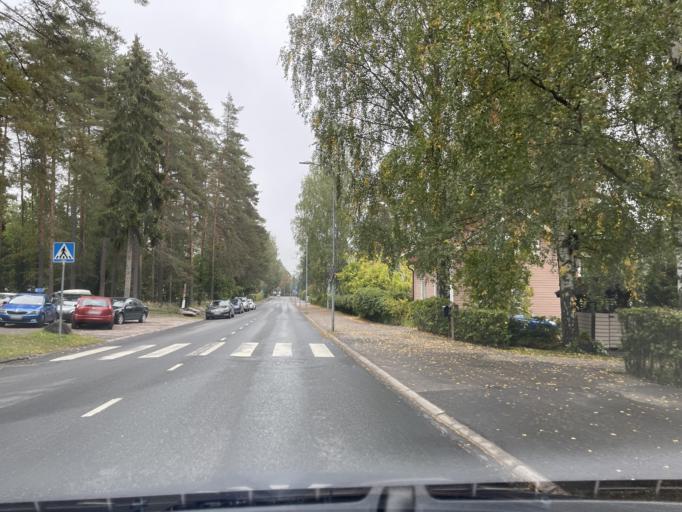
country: FI
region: Uusimaa
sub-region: Helsinki
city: Hyvinge
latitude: 60.6208
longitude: 24.8494
